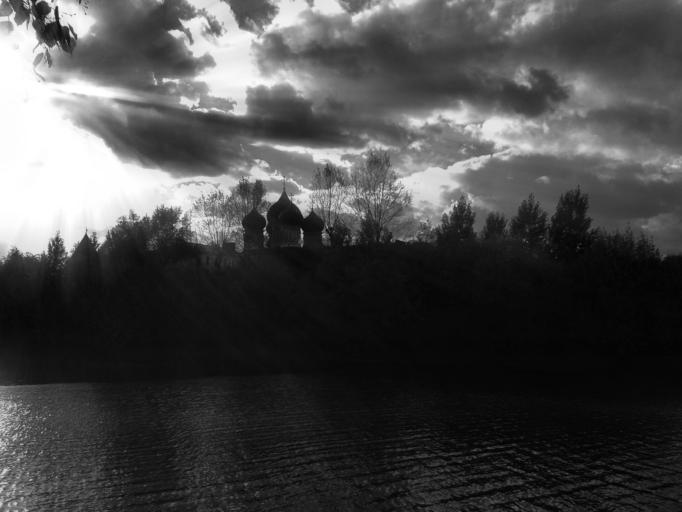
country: RU
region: Moscow
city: Metrogorodok
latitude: 55.7911
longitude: 37.7684
